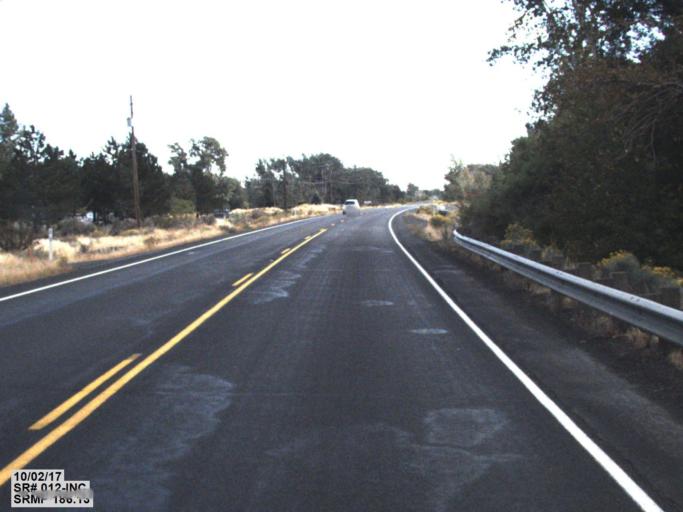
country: US
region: Washington
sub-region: Yakima County
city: Tieton
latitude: 46.7477
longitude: -120.7736
